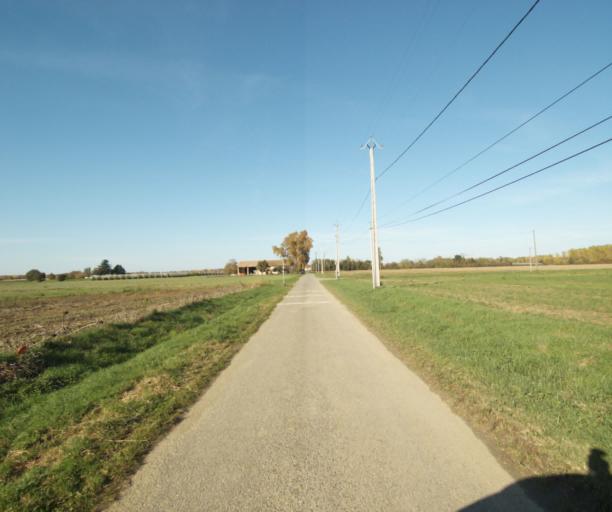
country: FR
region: Midi-Pyrenees
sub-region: Departement du Tarn-et-Garonne
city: Finhan
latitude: 43.9360
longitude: 1.2063
